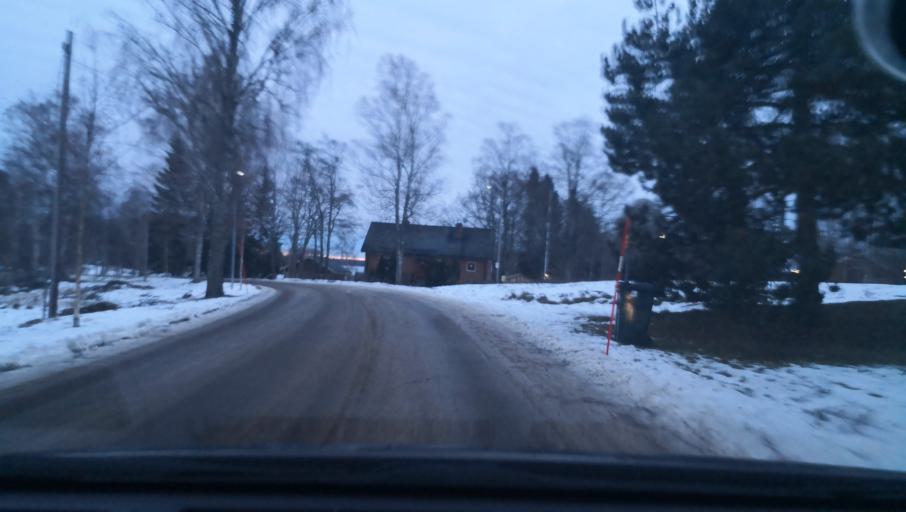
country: SE
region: Dalarna
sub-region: Avesta Kommun
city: Horndal
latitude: 60.2009
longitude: 16.4795
